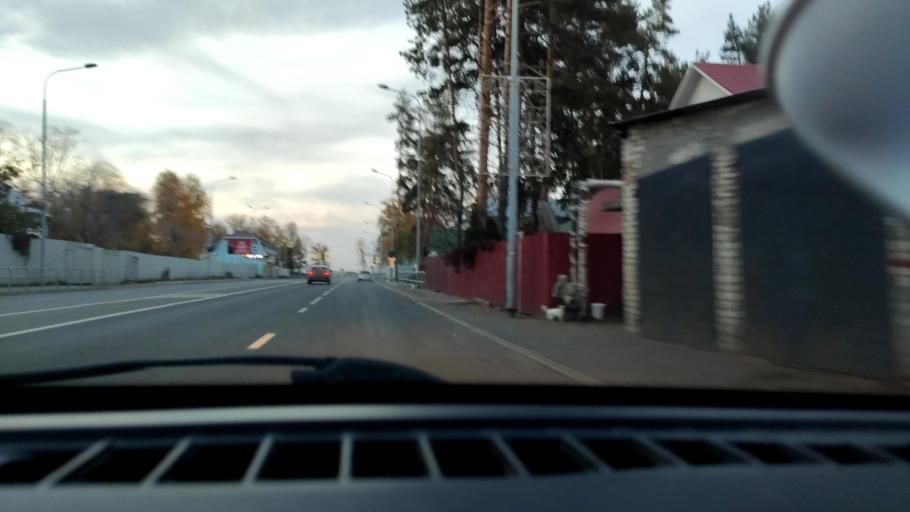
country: RU
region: Samara
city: Samara
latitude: 53.2656
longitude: 50.2425
